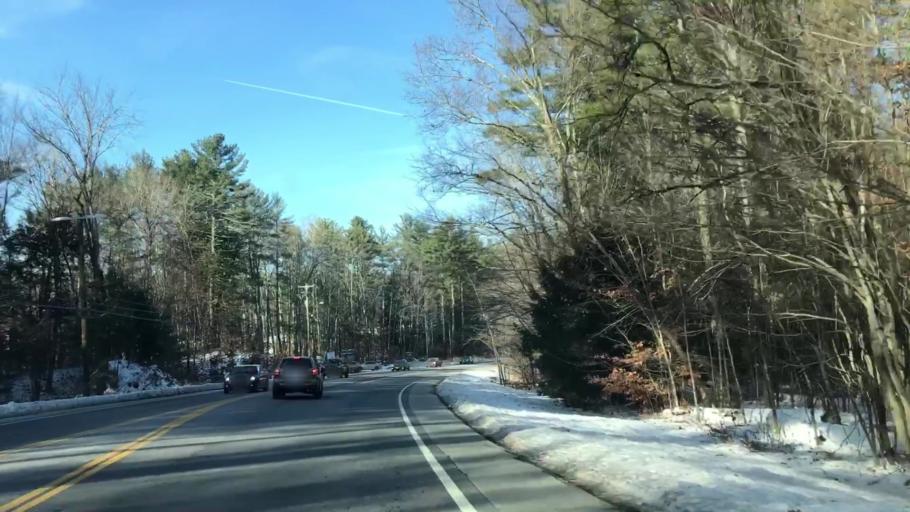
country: US
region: New Hampshire
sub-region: Hillsborough County
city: Mont Vernon
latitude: 42.8896
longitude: -71.6091
